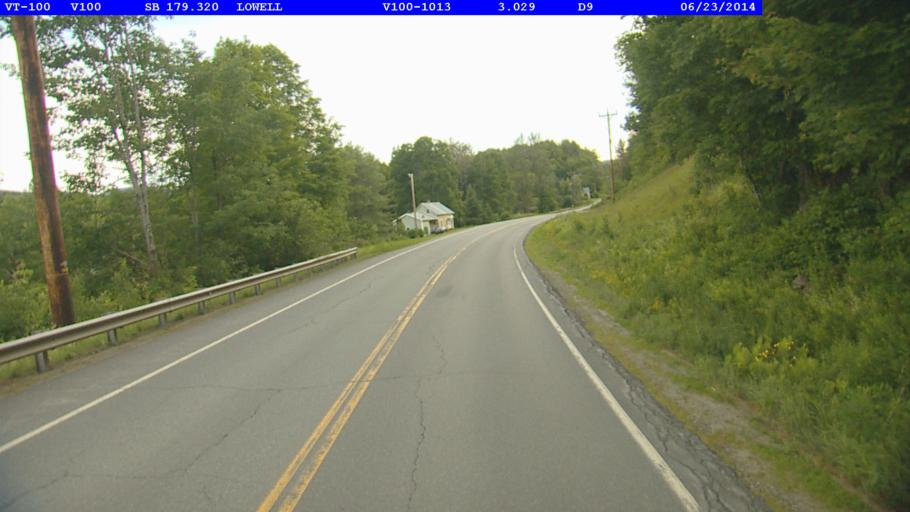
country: US
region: Vermont
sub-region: Lamoille County
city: Hyde Park
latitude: 44.7799
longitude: -72.4511
